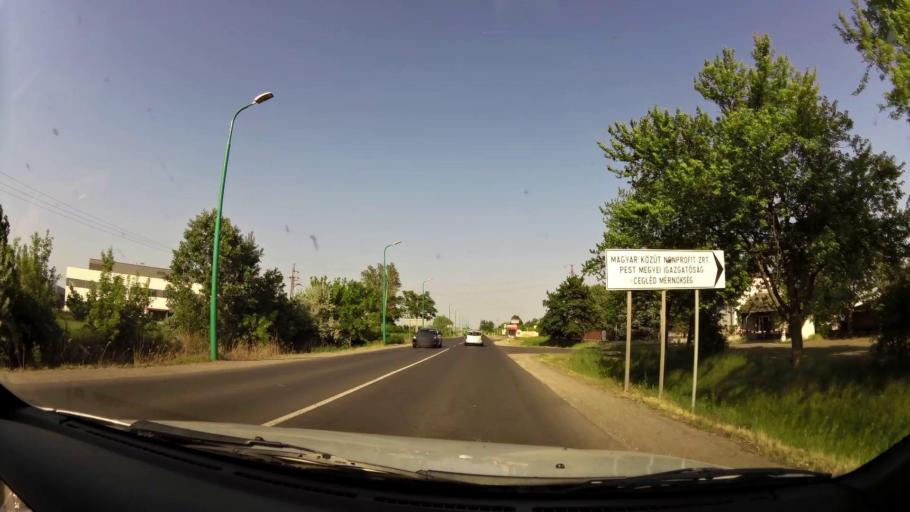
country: HU
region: Pest
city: Cegled
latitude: 47.1879
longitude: 19.8022
